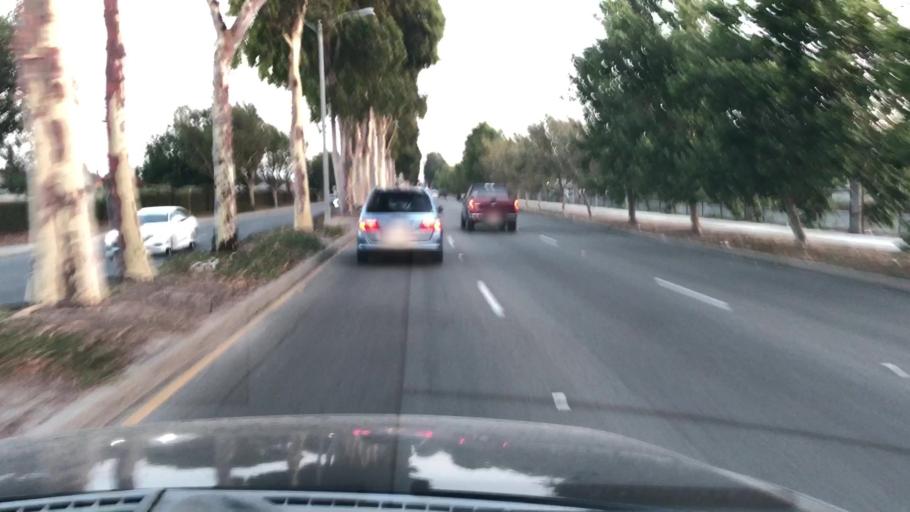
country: US
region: California
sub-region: Ventura County
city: Port Hueneme
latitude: 34.1675
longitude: -119.1951
